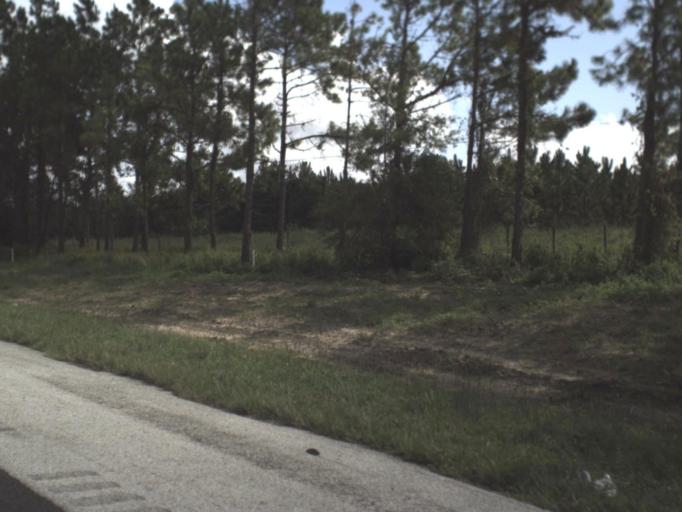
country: US
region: Florida
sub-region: Pasco County
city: Wesley Chapel
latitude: 28.2789
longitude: -82.3261
